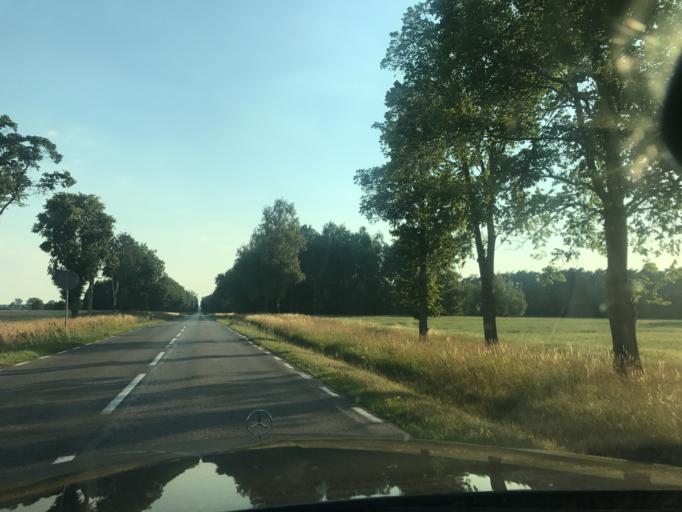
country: PL
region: Lublin Voivodeship
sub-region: Powiat parczewski
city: Jablon
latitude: 51.7292
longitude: 23.1174
